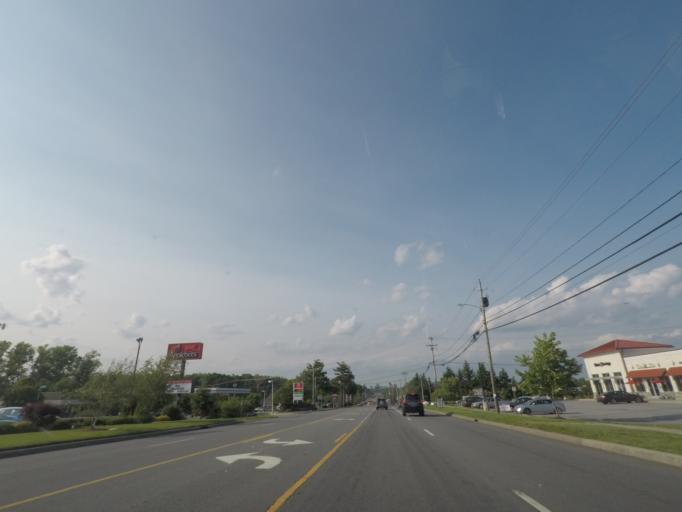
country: US
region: New York
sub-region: Orange County
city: Gardnertown
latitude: 41.4983
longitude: -74.0715
